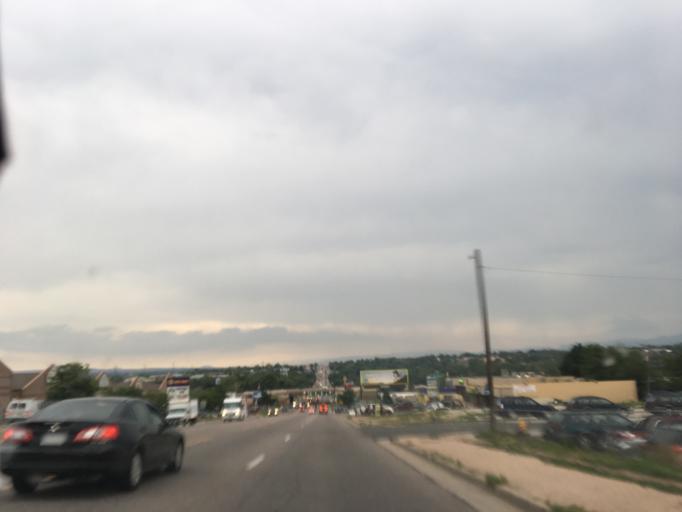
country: US
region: Colorado
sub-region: Arapahoe County
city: Sheridan
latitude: 39.6558
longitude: -105.0253
